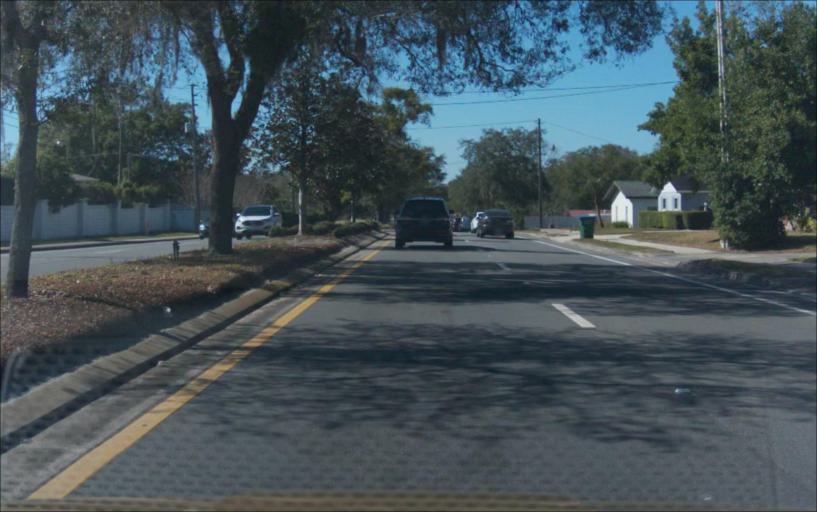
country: US
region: Florida
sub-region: Orange County
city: Winter Park
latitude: 28.6251
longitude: -81.3243
